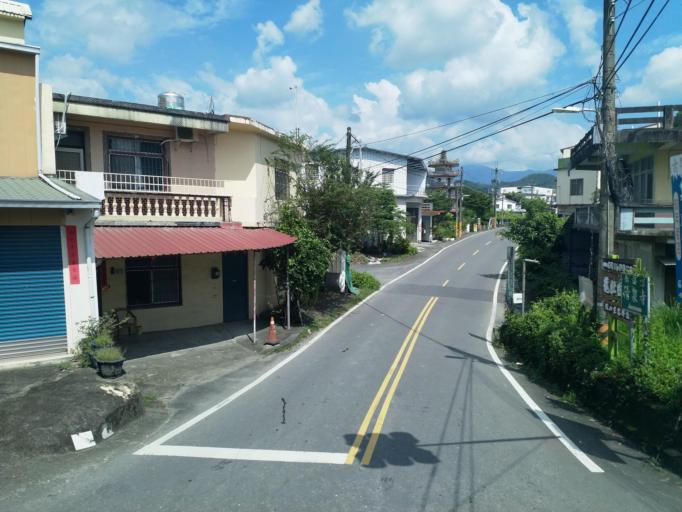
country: TW
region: Taiwan
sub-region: Pingtung
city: Pingtung
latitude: 22.8793
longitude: 120.5689
